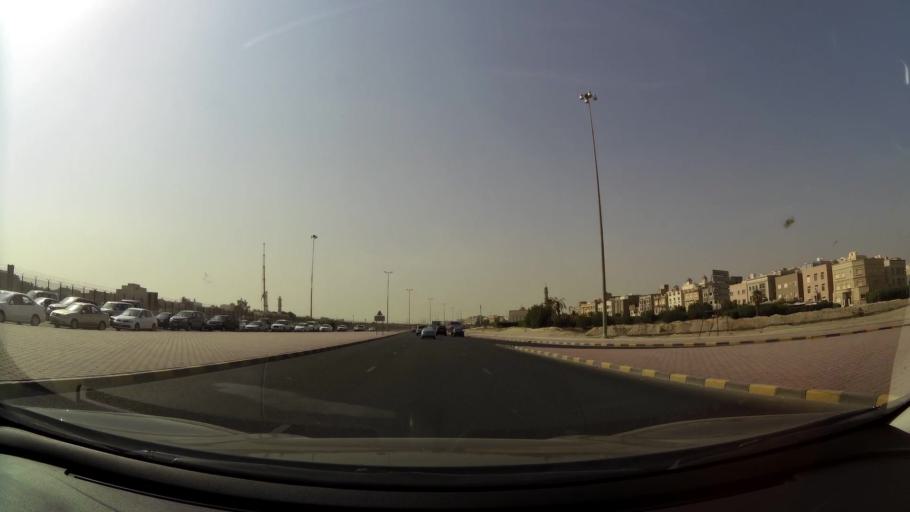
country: KW
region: Al Ahmadi
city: Al Manqaf
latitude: 29.1196
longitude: 48.1158
